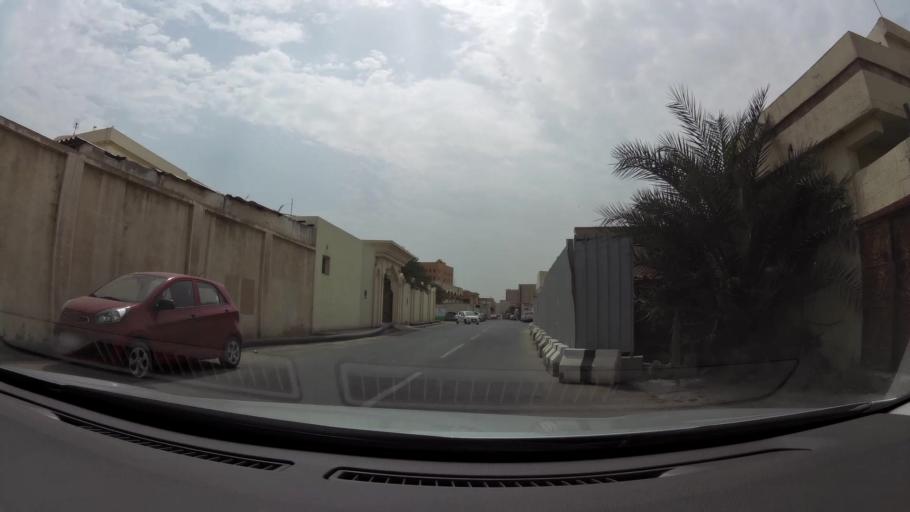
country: QA
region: Baladiyat ad Dawhah
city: Doha
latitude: 25.3063
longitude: 51.4975
